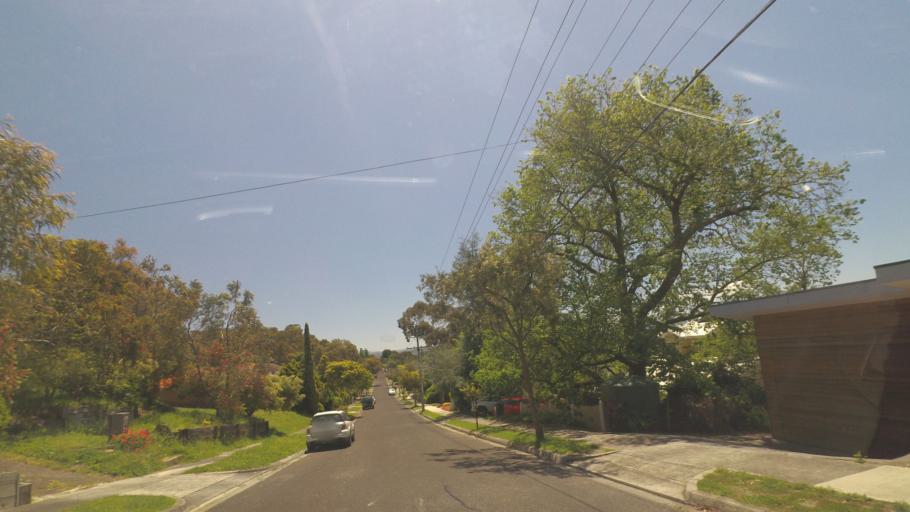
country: AU
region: Victoria
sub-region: Maroondah
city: Croydon North
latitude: -37.7692
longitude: 145.2852
